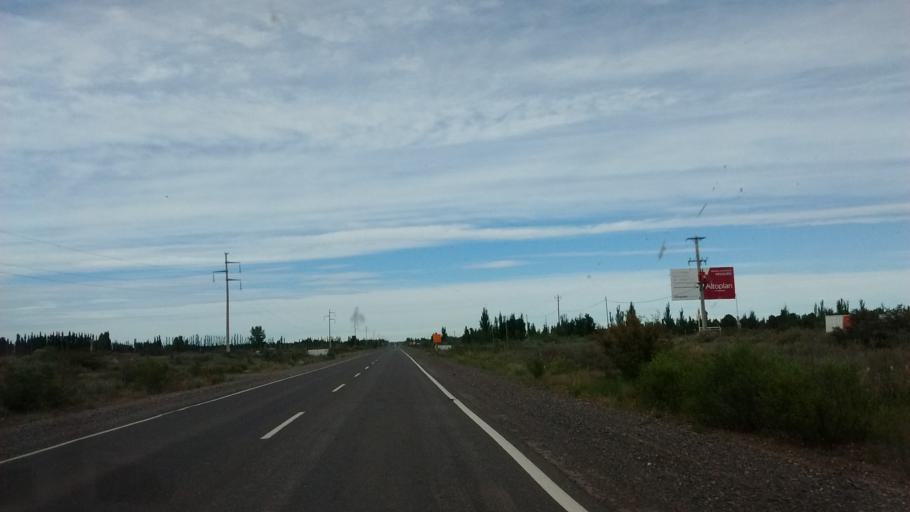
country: AR
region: Rio Negro
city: Contraalmirante Cordero
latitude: -38.6614
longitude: -68.1437
